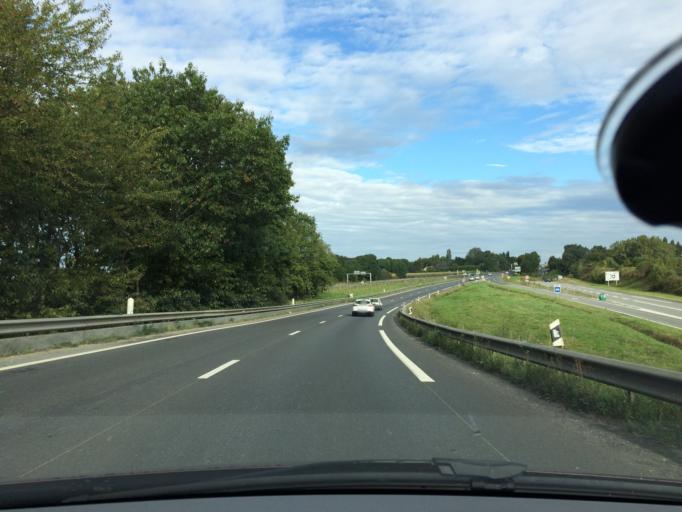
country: FR
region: Brittany
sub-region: Departement d'Ille-et-Vilaine
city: Saint-Jacques-de-la-Lande
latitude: 48.0800
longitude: -1.6947
